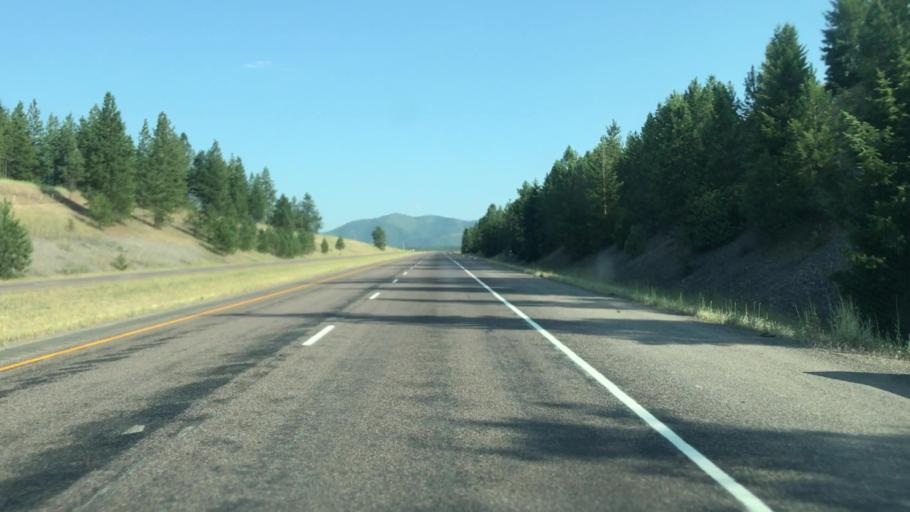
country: US
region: Montana
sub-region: Mineral County
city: Superior
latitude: 47.0523
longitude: -114.7580
